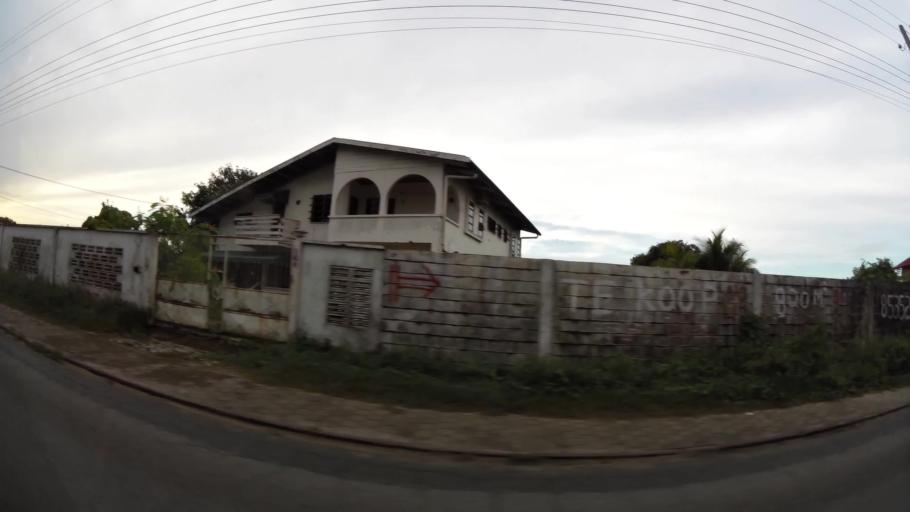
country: SR
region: Paramaribo
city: Paramaribo
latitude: 5.8220
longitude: -55.2016
